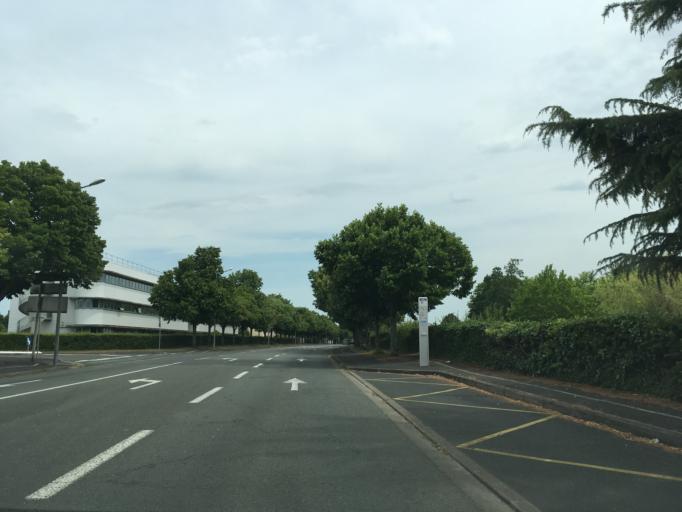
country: FR
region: Poitou-Charentes
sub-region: Departement des Deux-Sevres
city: Niort
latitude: 46.3115
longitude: -0.4773
